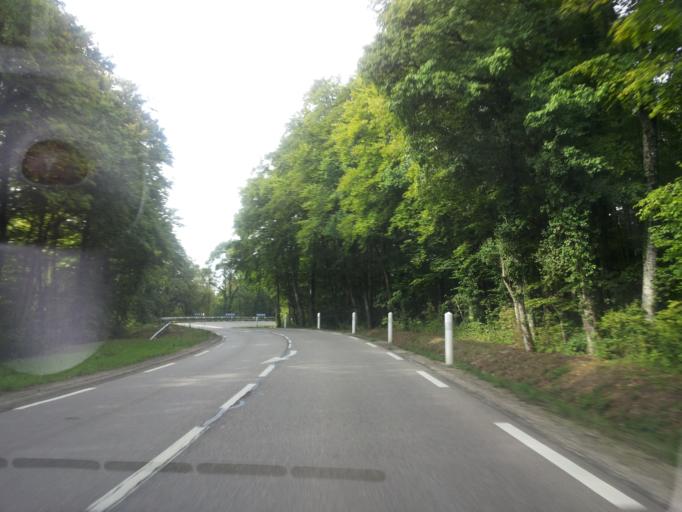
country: FR
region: Lorraine
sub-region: Departement des Vosges
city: Neufchateau
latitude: 48.3513
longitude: 5.7174
